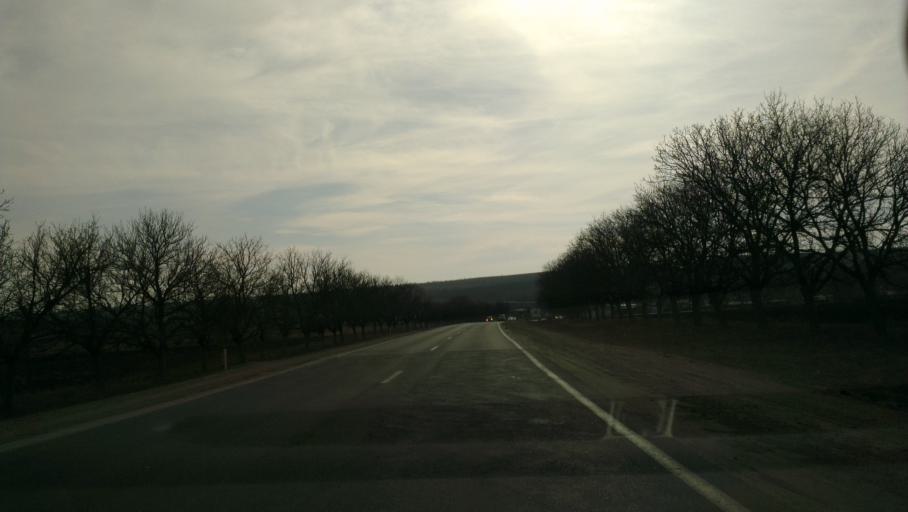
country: MD
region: Chisinau
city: Stauceni
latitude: 47.0899
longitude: 28.8371
